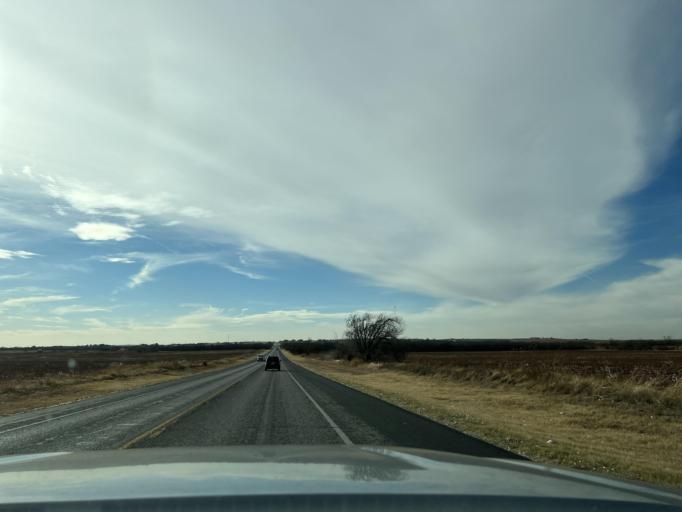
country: US
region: Texas
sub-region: Fisher County
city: Roby
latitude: 32.7498
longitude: -100.3542
